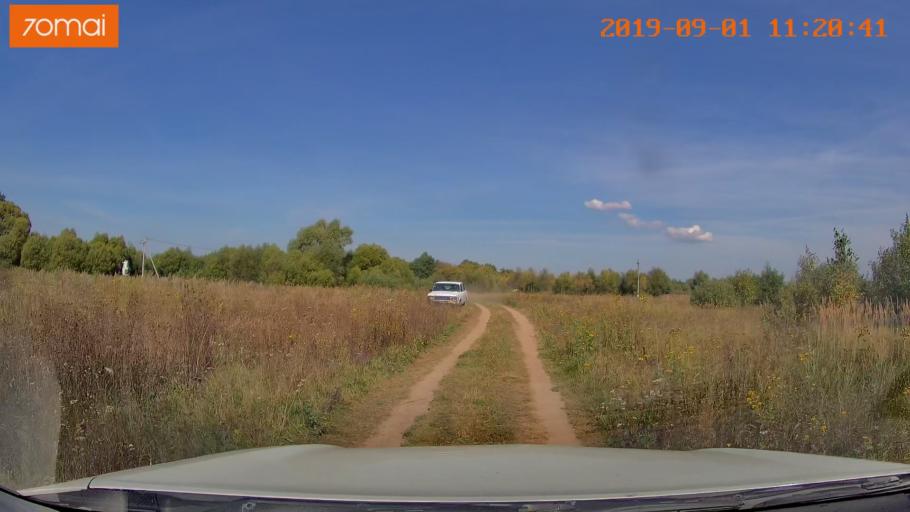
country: RU
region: Kaluga
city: Detchino
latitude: 54.8297
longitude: 36.3607
